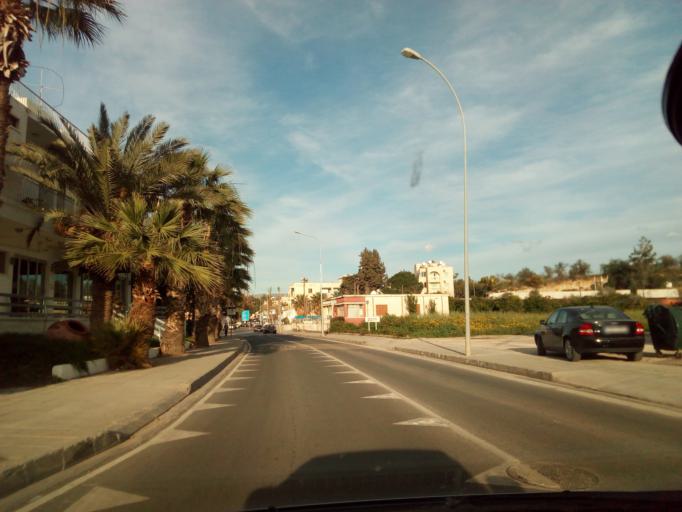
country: CY
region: Pafos
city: Polis
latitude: 35.0363
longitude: 32.4295
